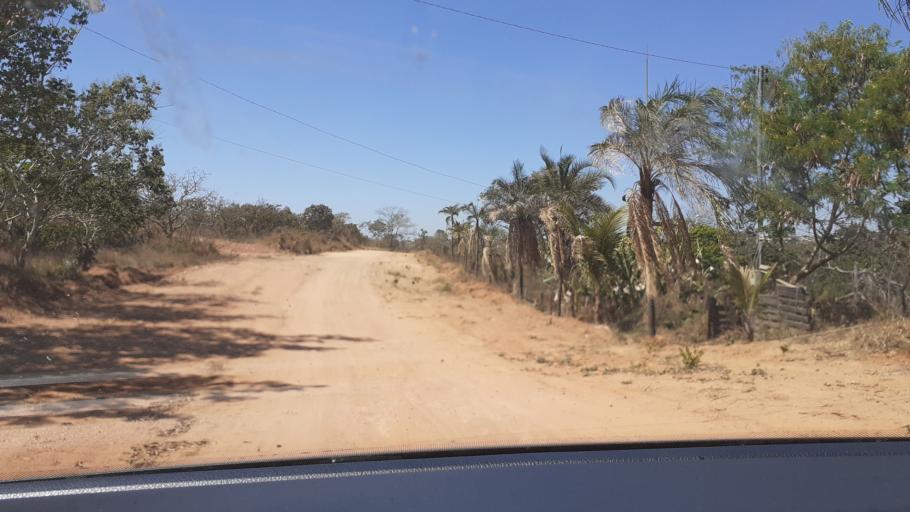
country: BR
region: Goias
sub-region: Caldas Novas
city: Caldas Novas
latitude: -17.7449
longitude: -48.6548
